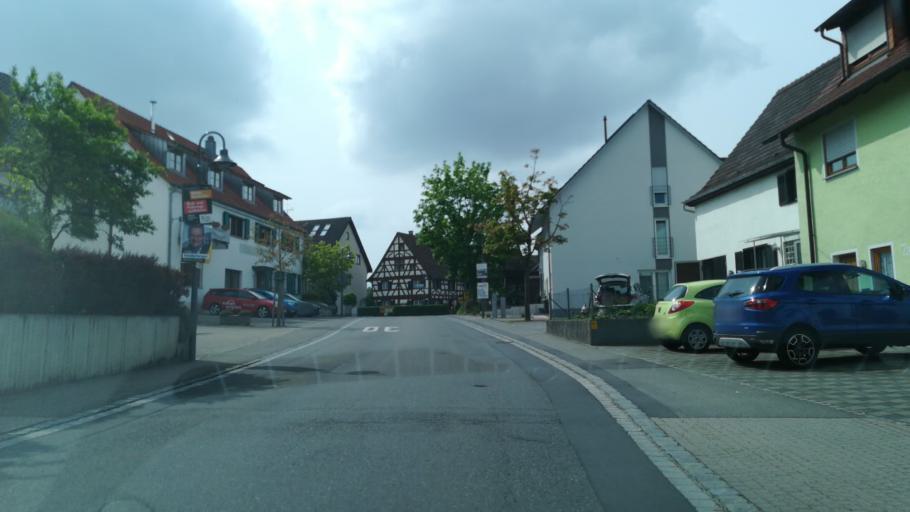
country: DE
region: Baden-Wuerttemberg
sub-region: Freiburg Region
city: Volkertshausen
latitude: 47.7862
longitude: 8.8761
